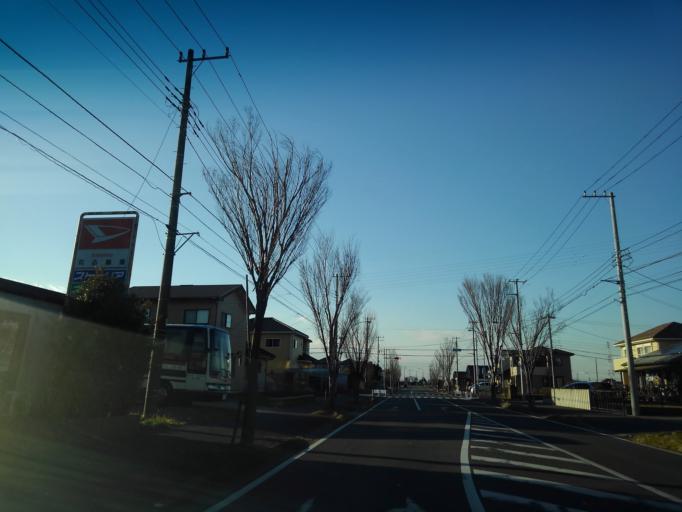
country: JP
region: Chiba
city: Kimitsu
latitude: 35.3118
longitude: 139.9184
